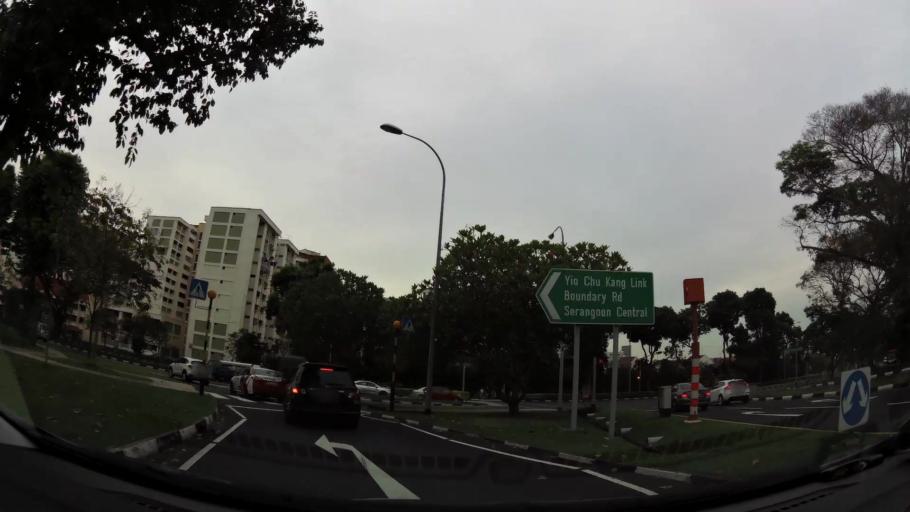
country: SG
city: Singapore
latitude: 1.3581
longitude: 103.8745
